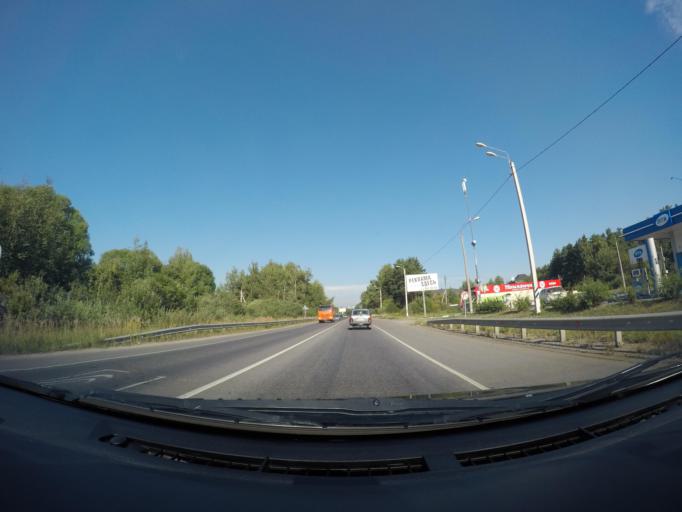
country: RU
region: Moskovskaya
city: Il'inskiy
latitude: 55.6420
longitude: 38.1566
